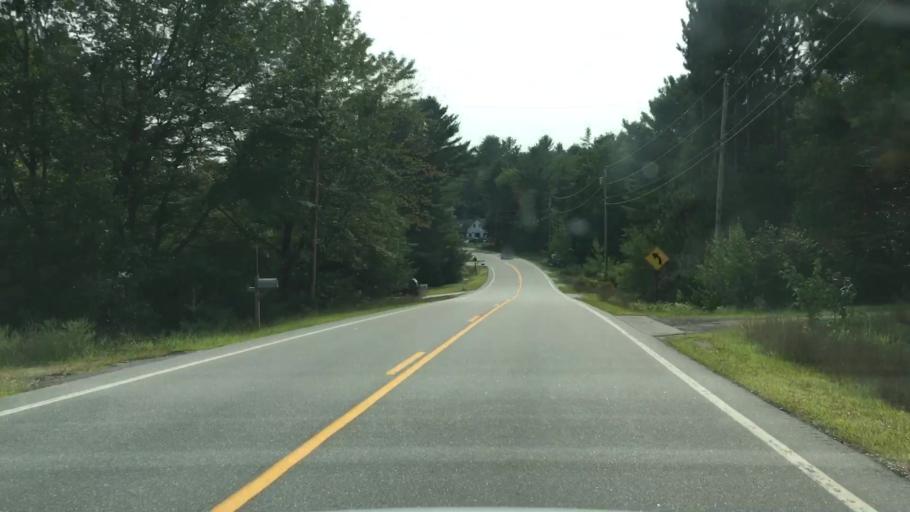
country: US
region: Maine
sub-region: Oxford County
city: Buckfield
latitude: 44.2810
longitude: -70.3788
